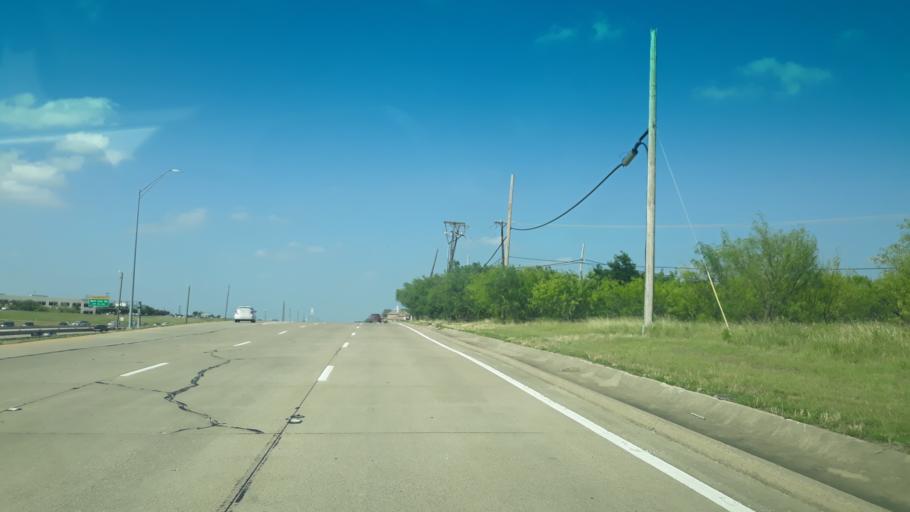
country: US
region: Texas
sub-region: Dallas County
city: Irving
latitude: 32.8599
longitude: -97.0087
